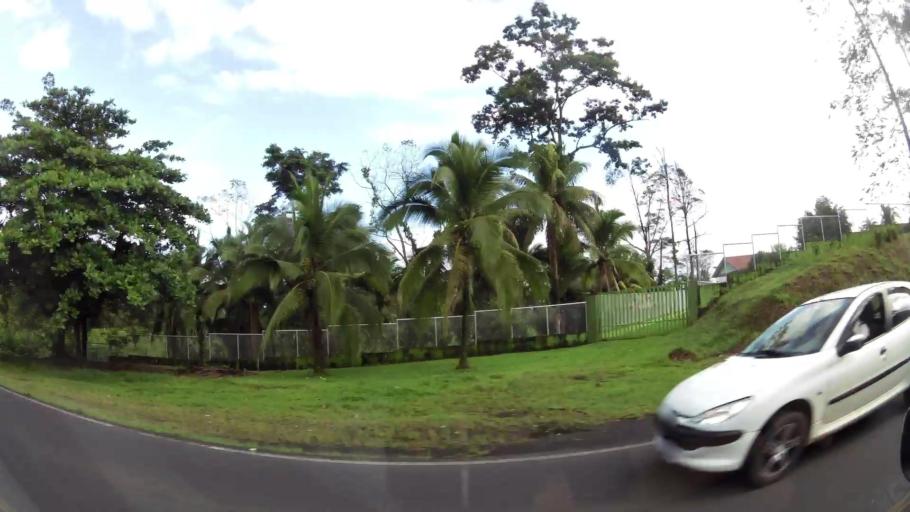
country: CR
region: Limon
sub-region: Canton de Guacimo
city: Guacimo
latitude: 10.1979
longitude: -83.6588
